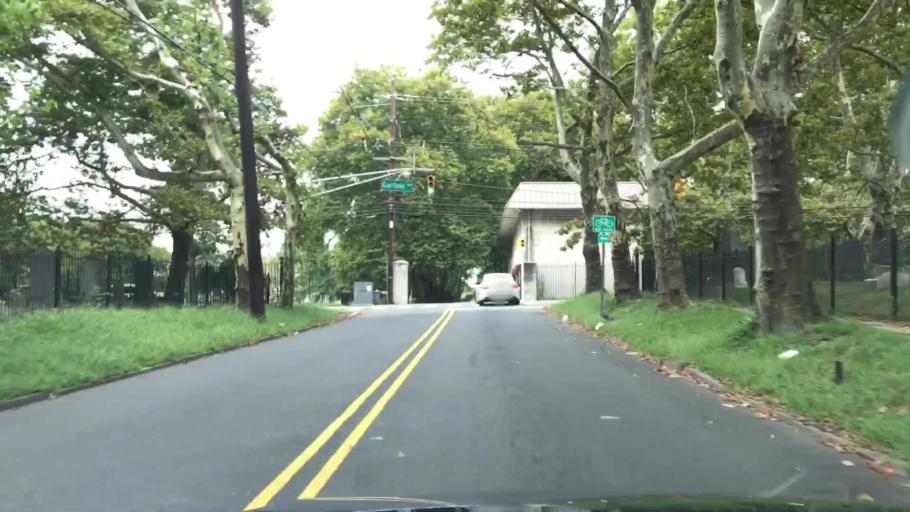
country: US
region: New Jersey
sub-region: Hudson County
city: Jersey City
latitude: 40.6960
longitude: -74.0850
